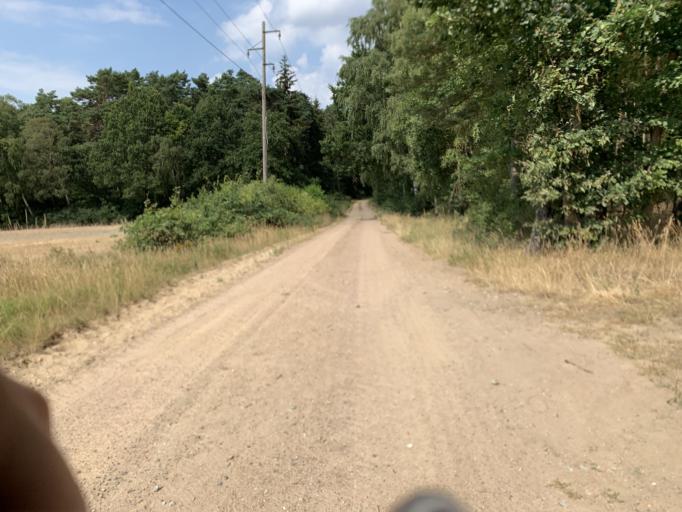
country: DE
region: Lower Saxony
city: Thomasburg
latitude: 53.2051
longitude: 10.6353
